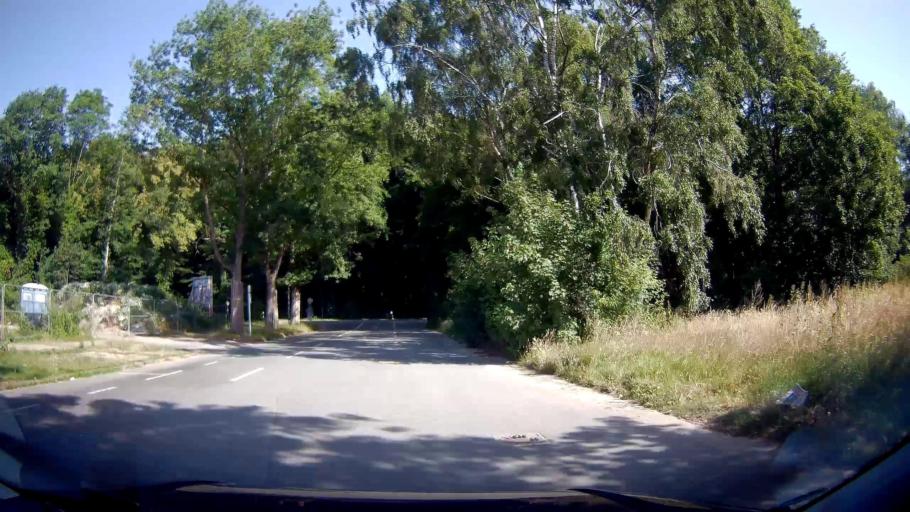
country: DE
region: North Rhine-Westphalia
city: Herten
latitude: 51.5879
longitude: 7.0787
